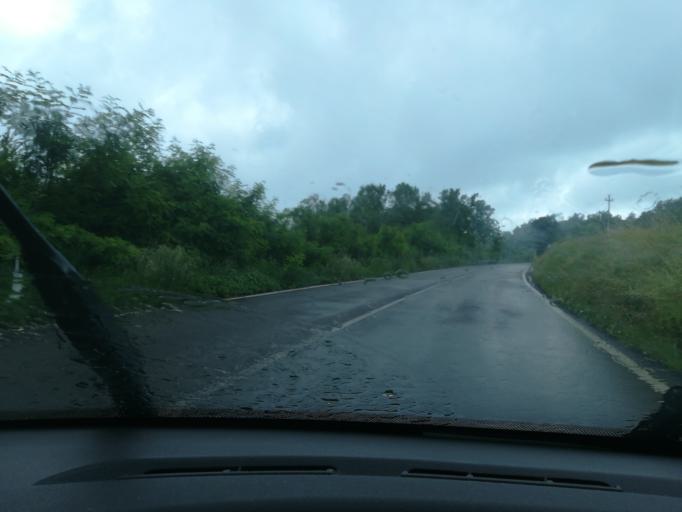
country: IT
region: The Marches
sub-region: Provincia di Macerata
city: Sarnano
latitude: 43.0087
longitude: 13.3276
